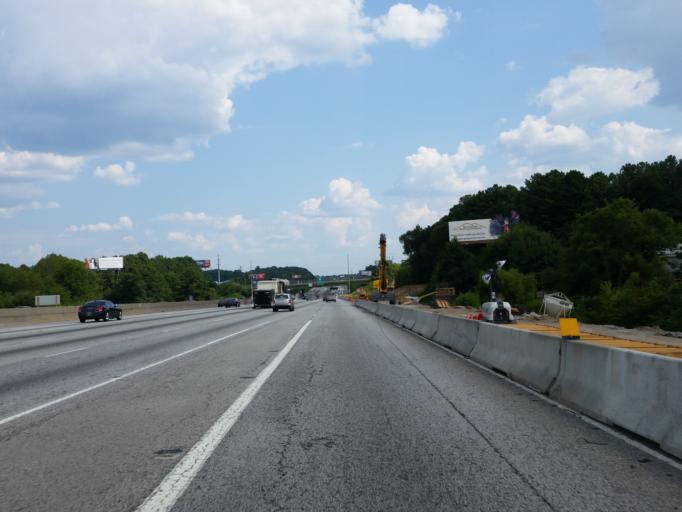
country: US
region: Georgia
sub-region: Cobb County
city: Marietta
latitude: 33.9758
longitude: -84.5339
